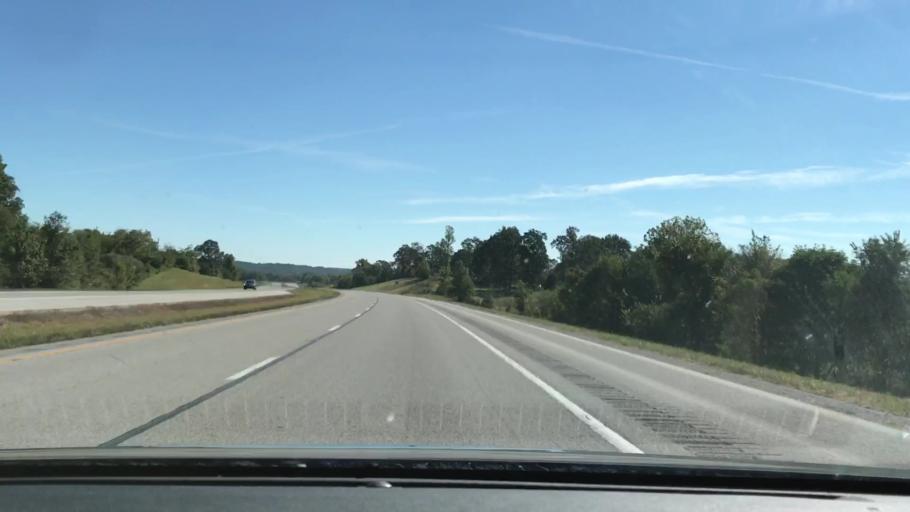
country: US
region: Kentucky
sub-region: Todd County
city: Elkton
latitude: 36.8211
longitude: -87.1906
